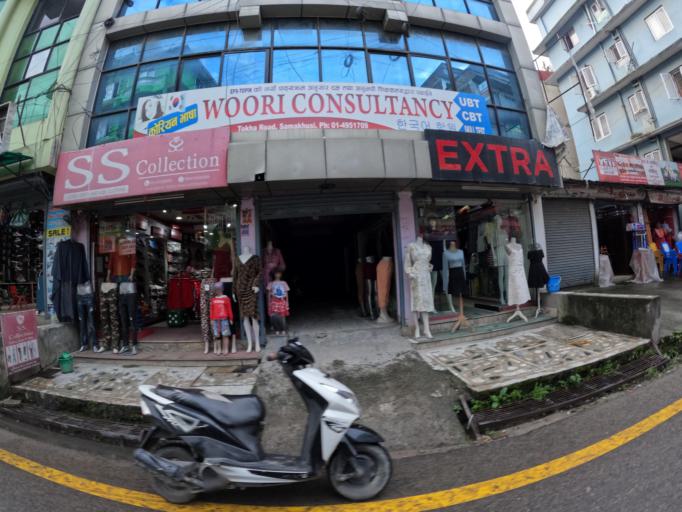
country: NP
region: Central Region
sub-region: Bagmati Zone
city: Kathmandu
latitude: 27.7363
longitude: 85.3190
